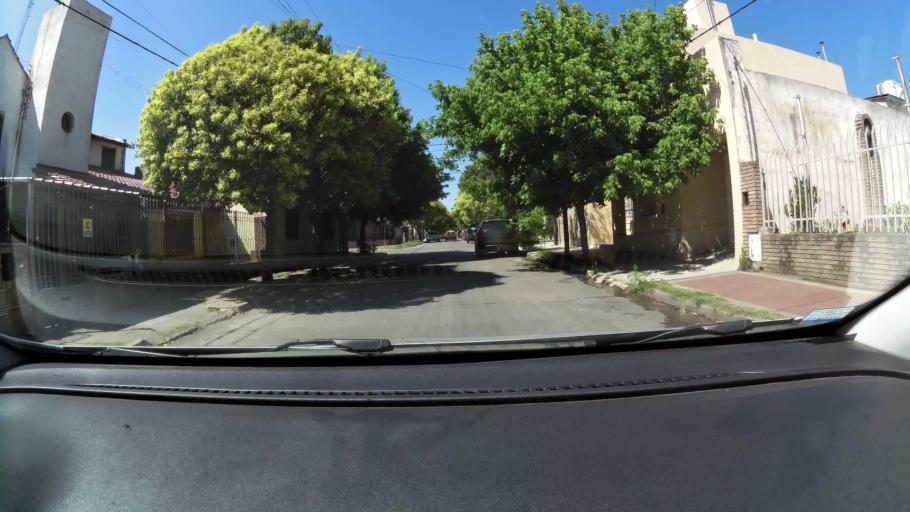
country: AR
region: Cordoba
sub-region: Departamento de Capital
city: Cordoba
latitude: -31.4168
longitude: -64.2129
